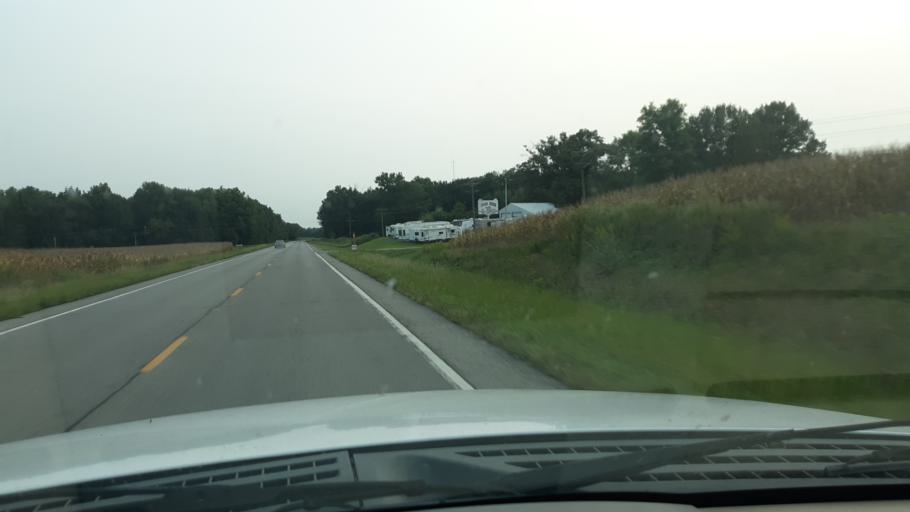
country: US
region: Illinois
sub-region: White County
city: Norris City
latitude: 37.9764
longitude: -88.3187
